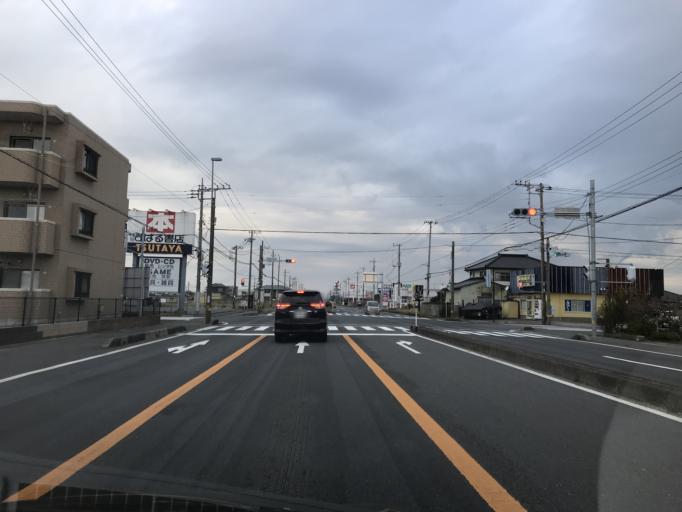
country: JP
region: Chiba
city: Omigawa
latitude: 35.8595
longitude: 140.7000
